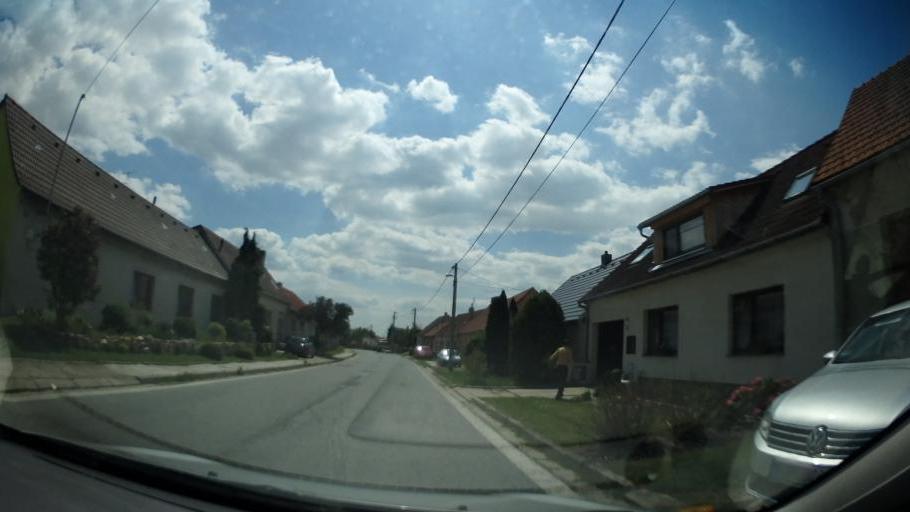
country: CZ
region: Vysocina
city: Hrotovice
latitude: 49.1345
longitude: 16.0803
